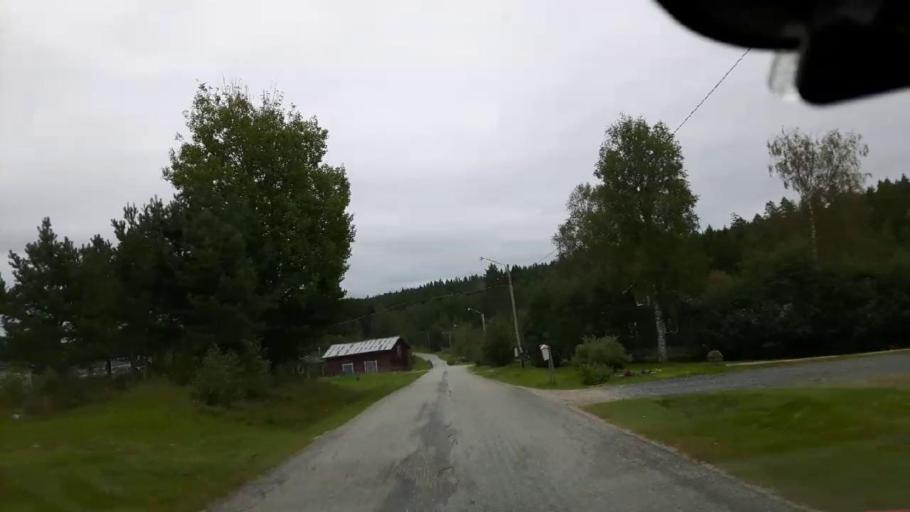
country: SE
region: Vaesternorrland
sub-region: Ange Kommun
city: Fransta
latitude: 62.7750
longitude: 15.9885
